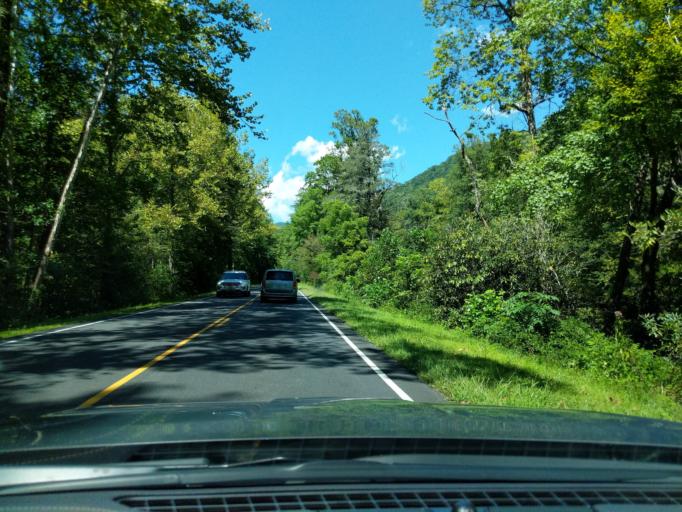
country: US
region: North Carolina
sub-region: Swain County
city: Cherokee
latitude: 35.5495
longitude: -83.3093
